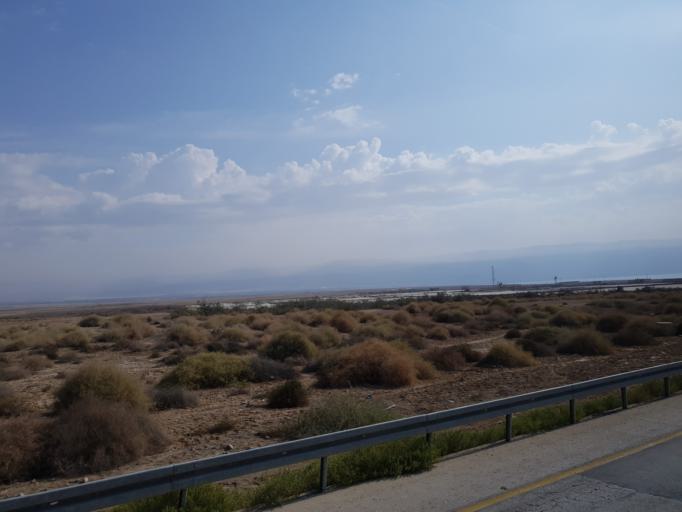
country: PS
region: West Bank
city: Jericho
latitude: 31.7792
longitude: 35.5031
